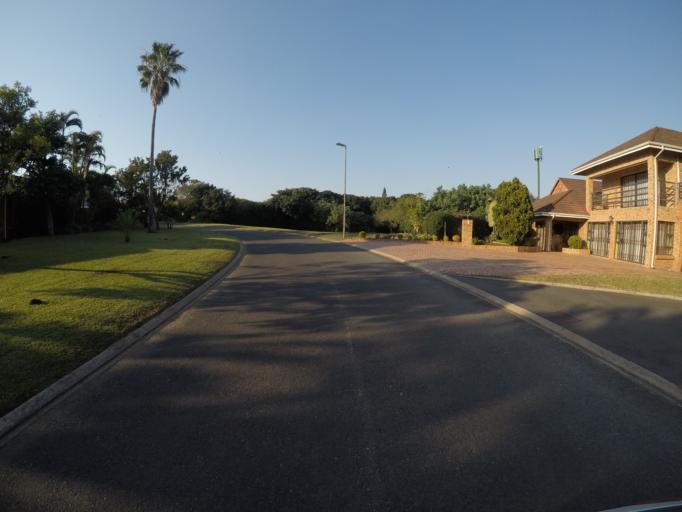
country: ZA
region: KwaZulu-Natal
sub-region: uThungulu District Municipality
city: Richards Bay
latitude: -28.7719
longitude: 32.1145
